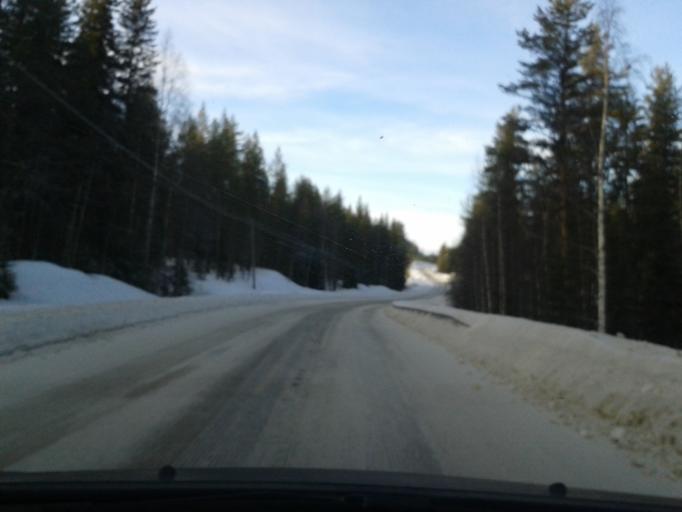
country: SE
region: Vaesternorrland
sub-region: OErnskoeldsviks Kommun
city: Bredbyn
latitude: 63.6669
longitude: 17.8314
